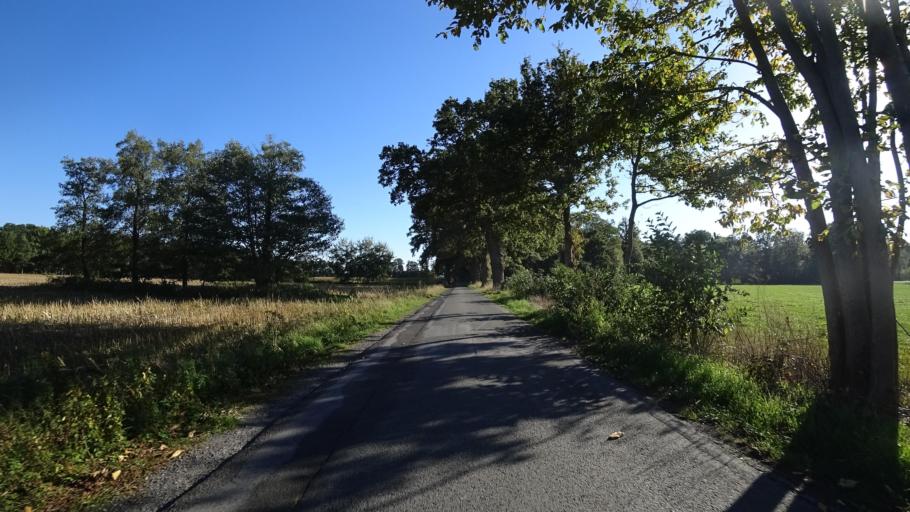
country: DE
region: North Rhine-Westphalia
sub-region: Regierungsbezirk Detmold
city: Guetersloh
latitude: 51.8796
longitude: 8.3581
